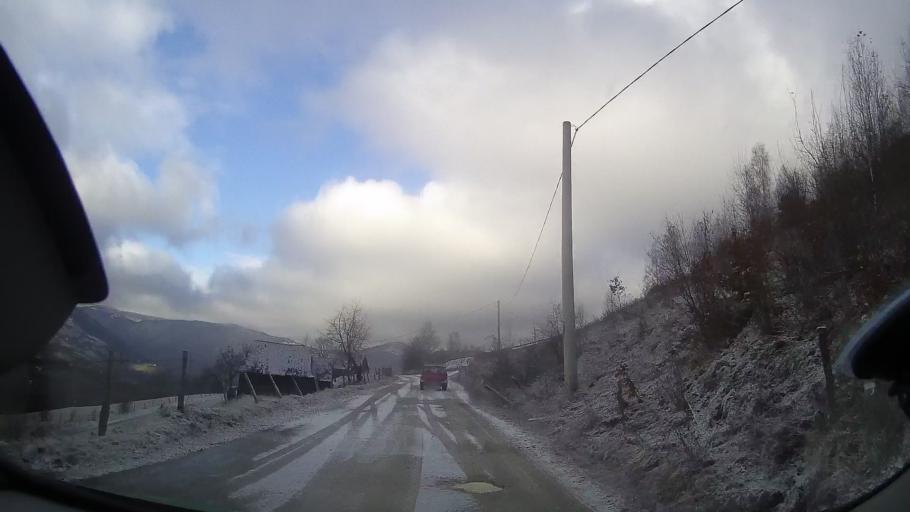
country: RO
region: Cluj
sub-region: Comuna Valea Ierii
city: Valea Ierii
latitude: 46.6724
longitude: 23.3228
